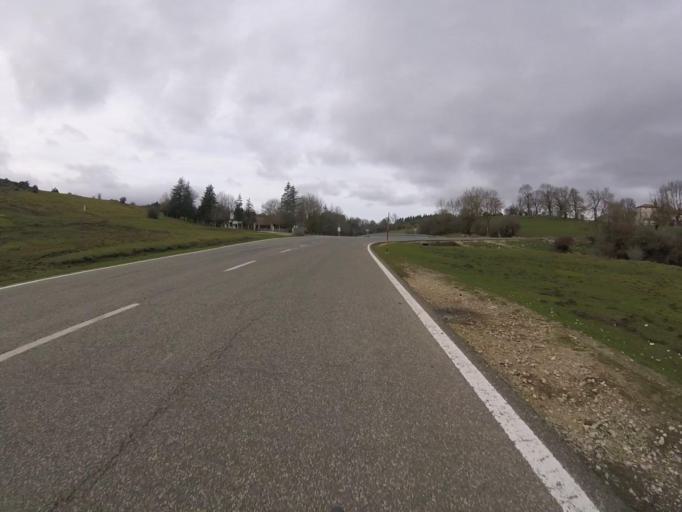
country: ES
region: Navarre
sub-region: Provincia de Navarra
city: Eulate
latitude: 42.8165
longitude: -2.1658
